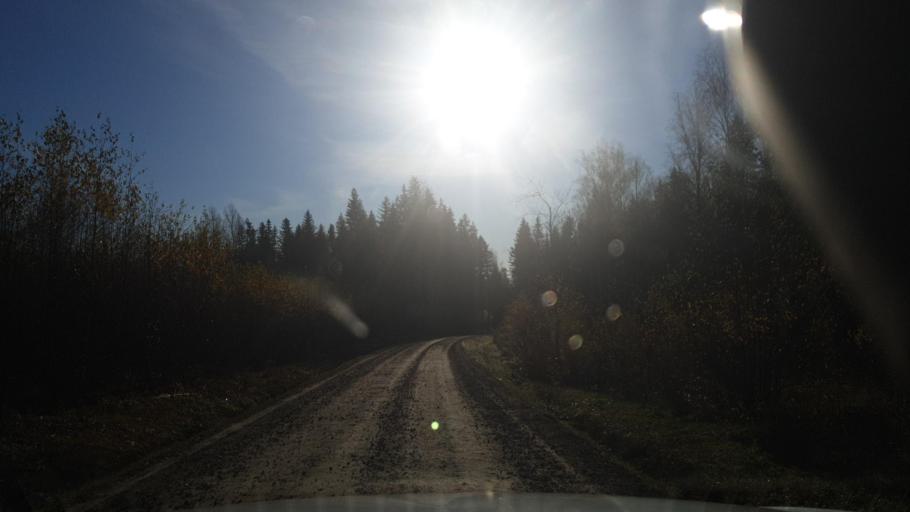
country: SE
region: Vaermland
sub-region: Karlstads Kommun
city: Edsvalla
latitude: 59.5183
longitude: 13.0090
